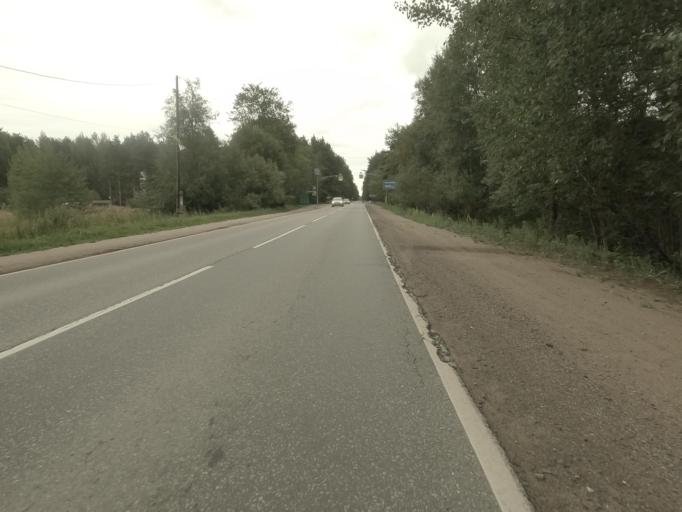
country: RU
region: Leningrad
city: Koltushi
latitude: 59.8926
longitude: 30.7419
